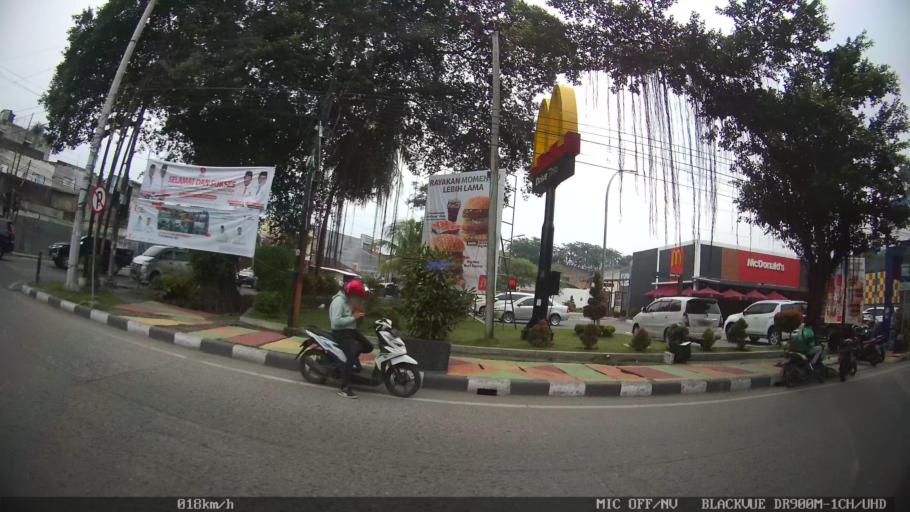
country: ID
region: North Sumatra
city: Medan
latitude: 3.5627
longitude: 98.6932
